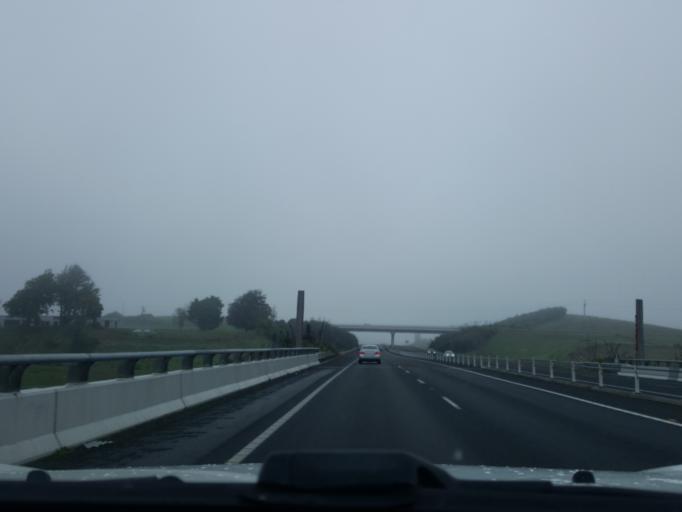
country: NZ
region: Waikato
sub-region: Waikato District
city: Ngaruawahia
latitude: -37.6993
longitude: 175.2108
